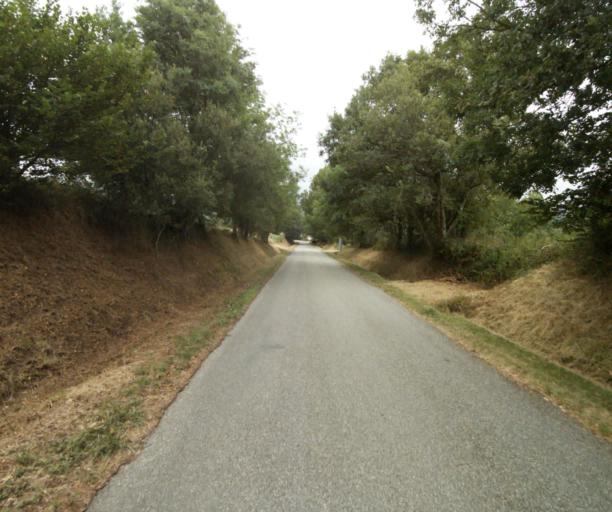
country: FR
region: Midi-Pyrenees
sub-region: Departement du Tarn
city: Soreze
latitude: 43.4062
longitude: 2.0858
